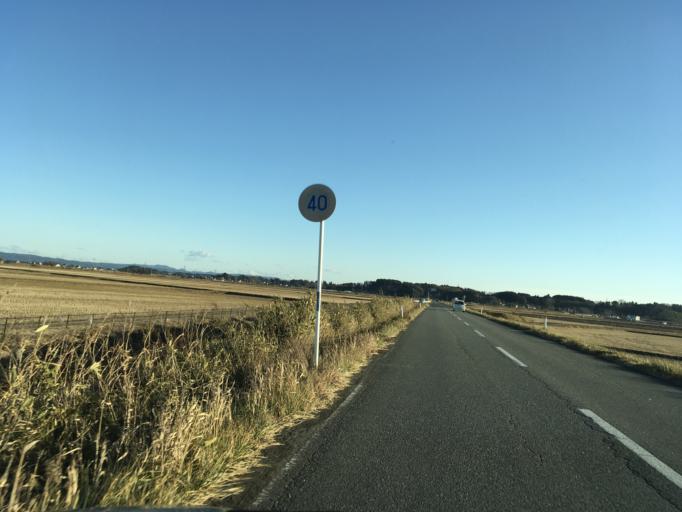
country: JP
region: Miyagi
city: Wakuya
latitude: 38.7299
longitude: 141.1253
